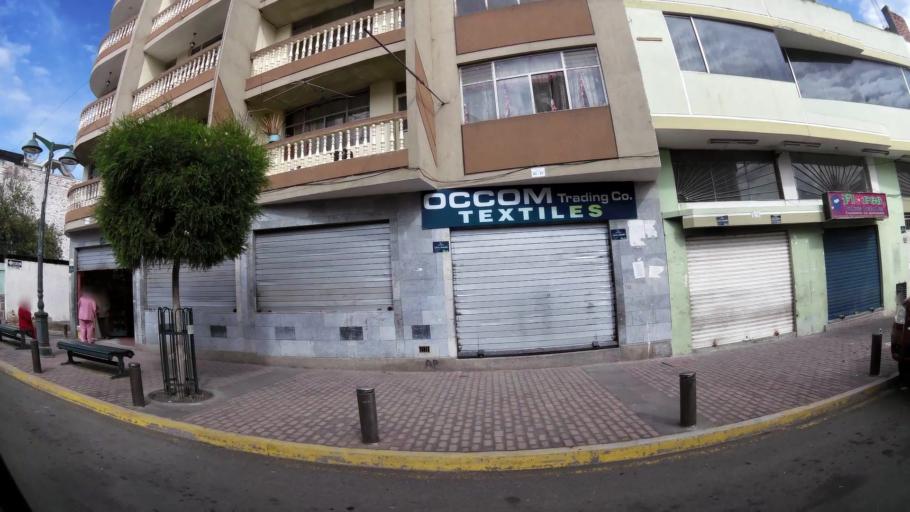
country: EC
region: Tungurahua
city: Ambato
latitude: -1.2483
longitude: -78.6407
